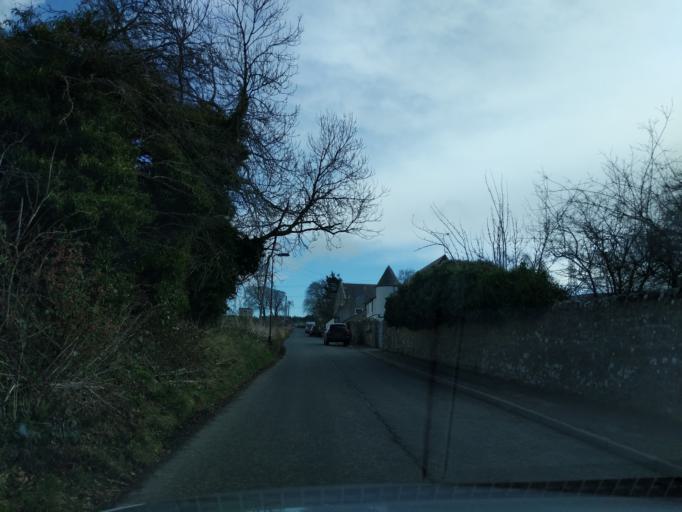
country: GB
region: Scotland
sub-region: Edinburgh
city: Balerno
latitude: 55.8772
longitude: -3.3269
